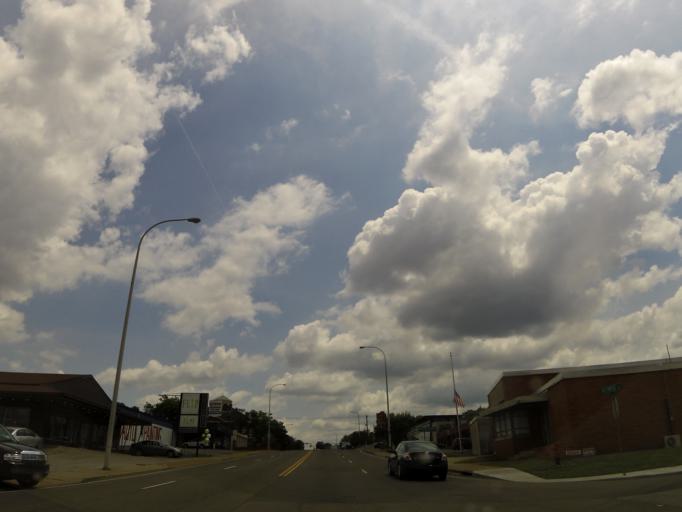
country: US
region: Tennessee
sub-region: Davidson County
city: Nashville
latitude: 36.1437
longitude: -86.7789
